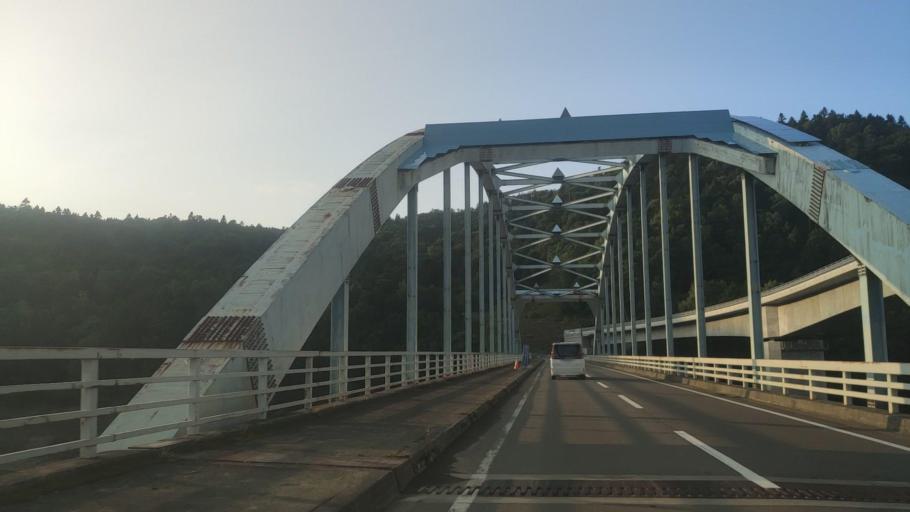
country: JP
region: Hokkaido
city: Bibai
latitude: 43.2355
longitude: 142.0371
